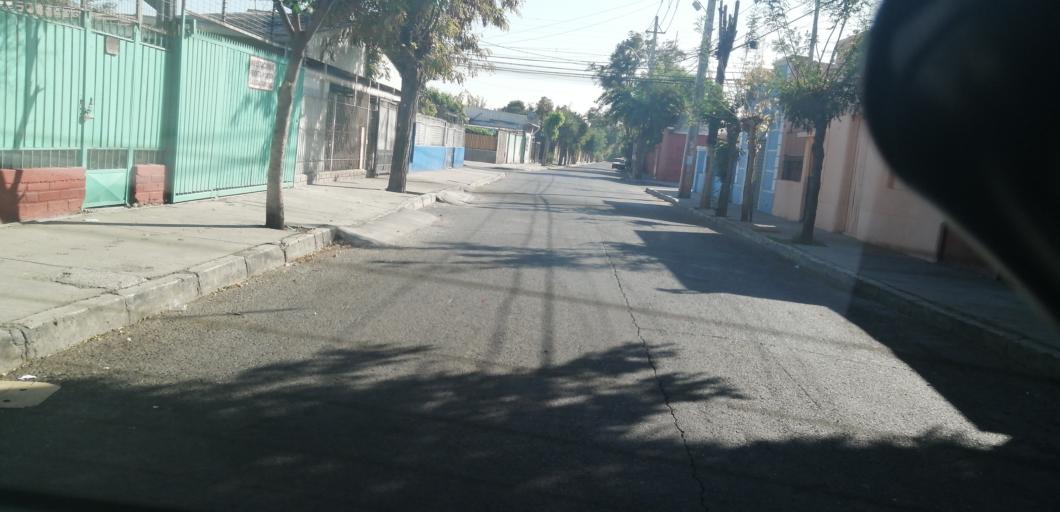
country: CL
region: Santiago Metropolitan
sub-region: Provincia de Santiago
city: Lo Prado
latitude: -33.4333
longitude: -70.7676
